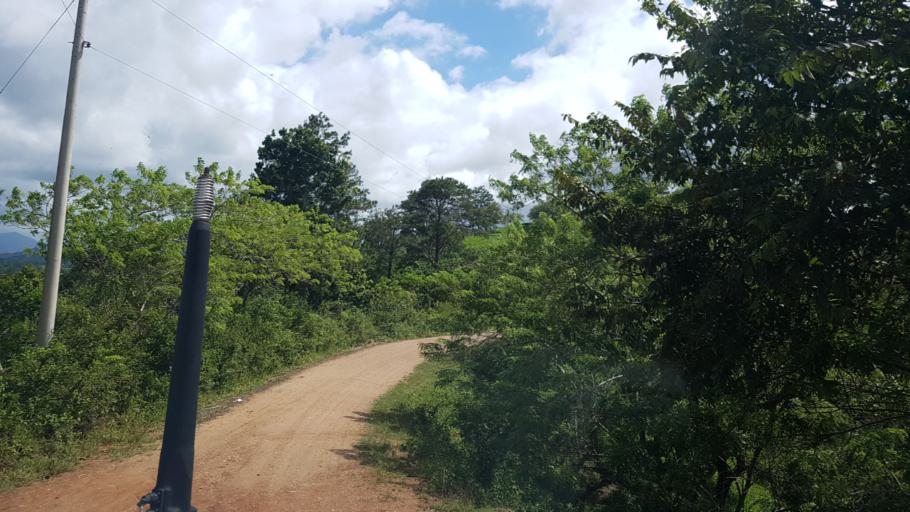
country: NI
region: Nueva Segovia
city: Ciudad Antigua
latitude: 13.6522
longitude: -86.2427
